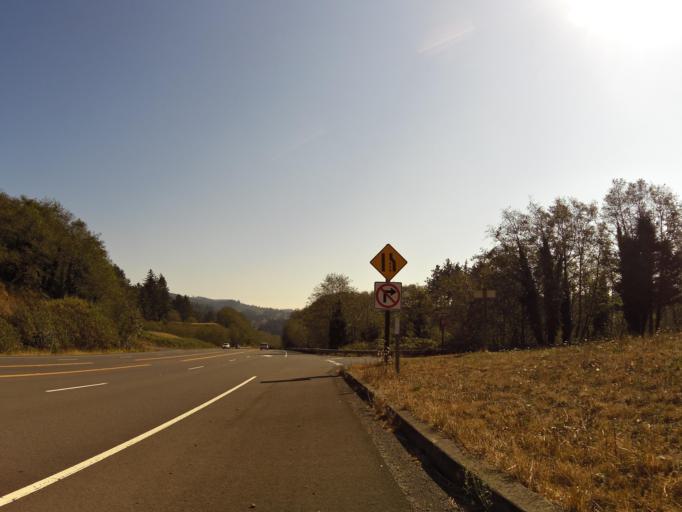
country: US
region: Oregon
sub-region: Tillamook County
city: Pacific City
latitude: 45.1415
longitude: -123.9693
